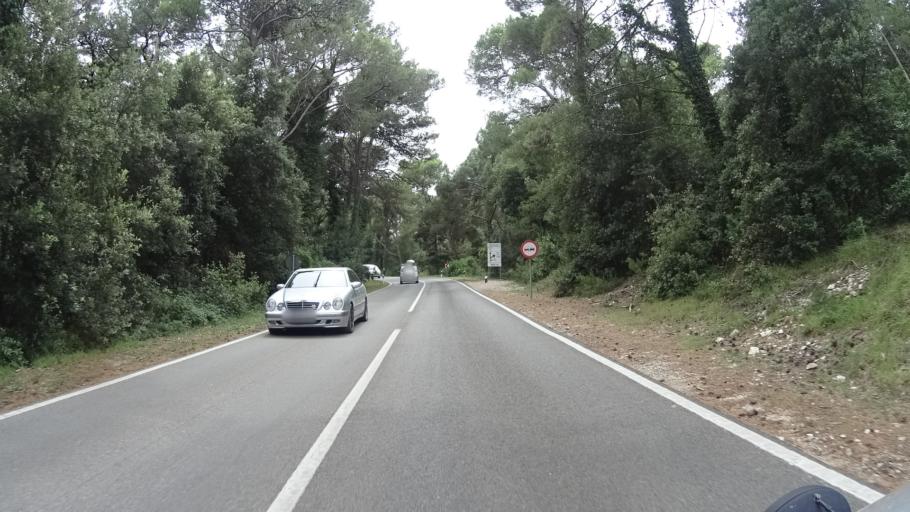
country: HR
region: Istarska
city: Medulin
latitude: 44.8108
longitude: 13.9093
